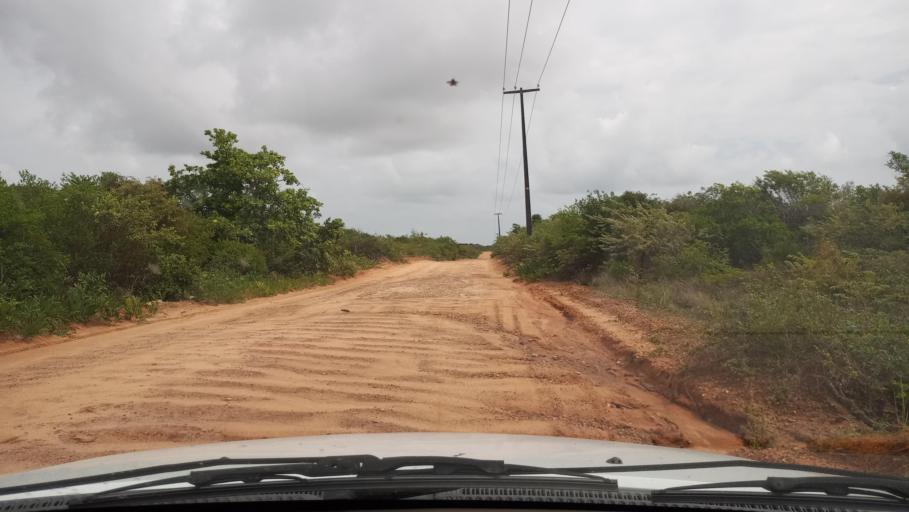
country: BR
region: Rio Grande do Norte
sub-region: Maxaranguape
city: Sao Miguel
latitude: -5.4774
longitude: -35.3022
